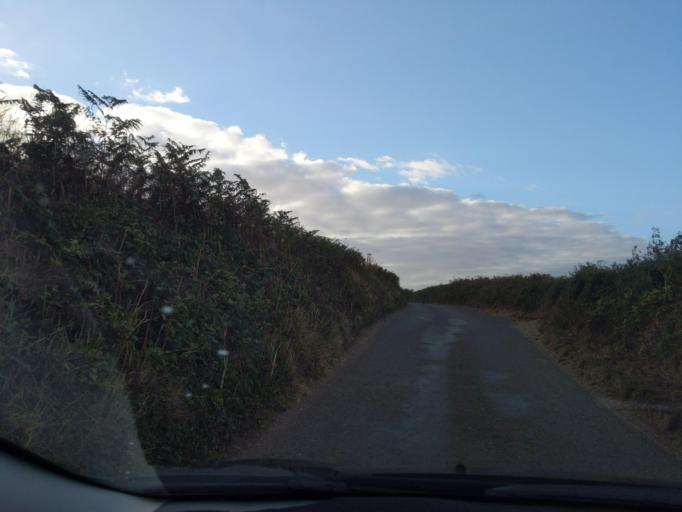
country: GB
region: England
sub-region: Devon
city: Salcombe
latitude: 50.2312
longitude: -3.8144
